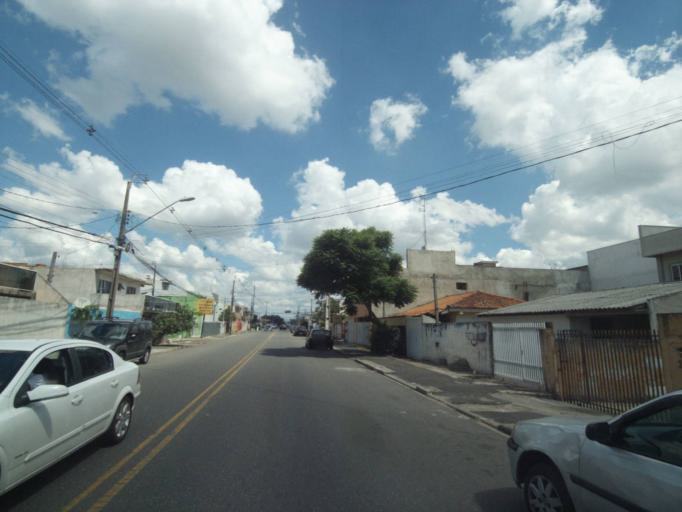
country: BR
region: Parana
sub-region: Pinhais
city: Pinhais
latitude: -25.4546
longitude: -49.2026
